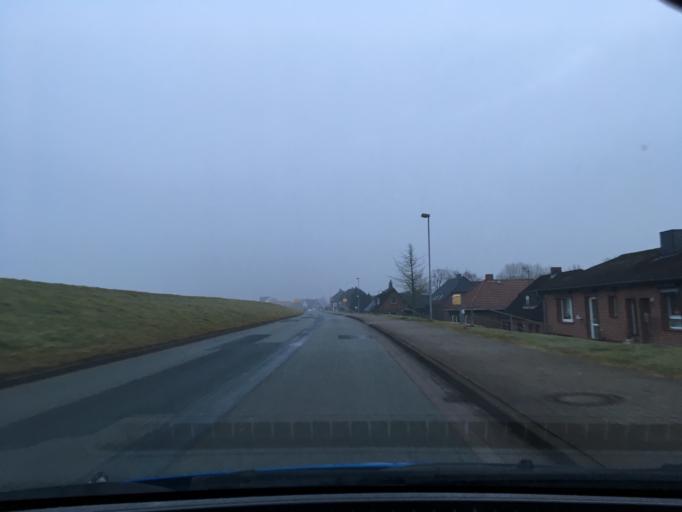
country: DE
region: Lower Saxony
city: Stelle
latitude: 53.4090
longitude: 10.1454
